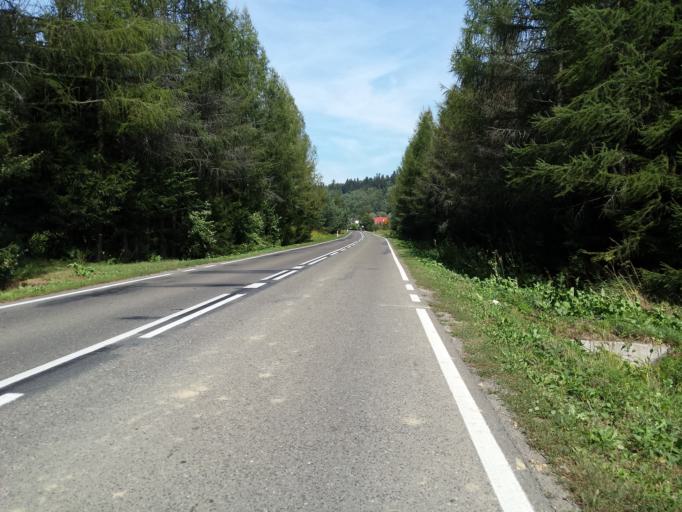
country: PL
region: Subcarpathian Voivodeship
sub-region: Powiat leski
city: Lesko
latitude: 49.4444
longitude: 22.3482
